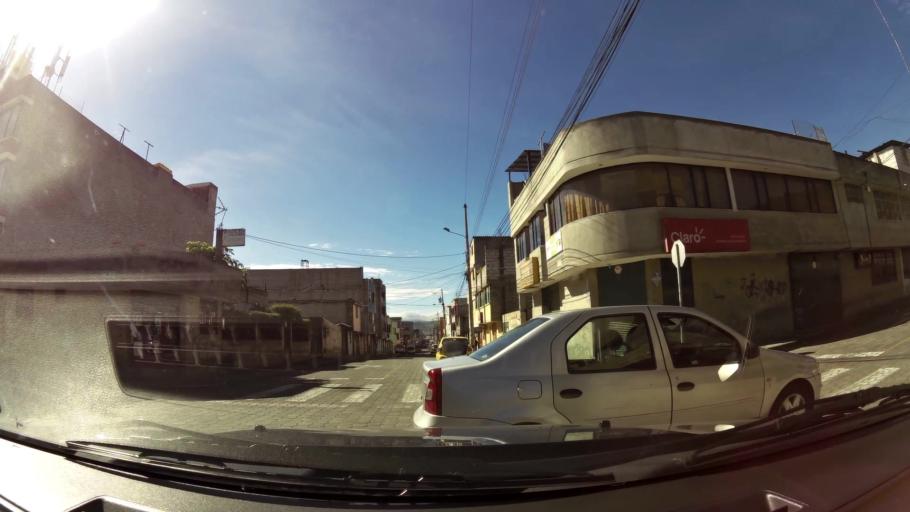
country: EC
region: Pichincha
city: Quito
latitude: -0.2988
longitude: -78.5669
